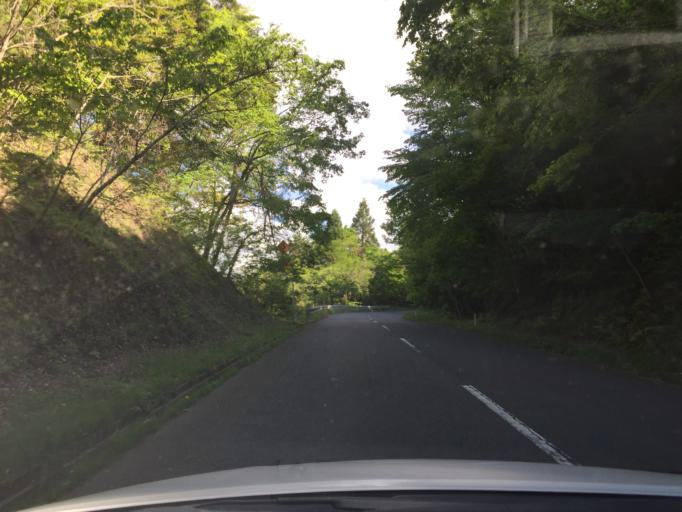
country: JP
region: Miyagi
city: Marumori
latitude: 37.7335
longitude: 140.8026
